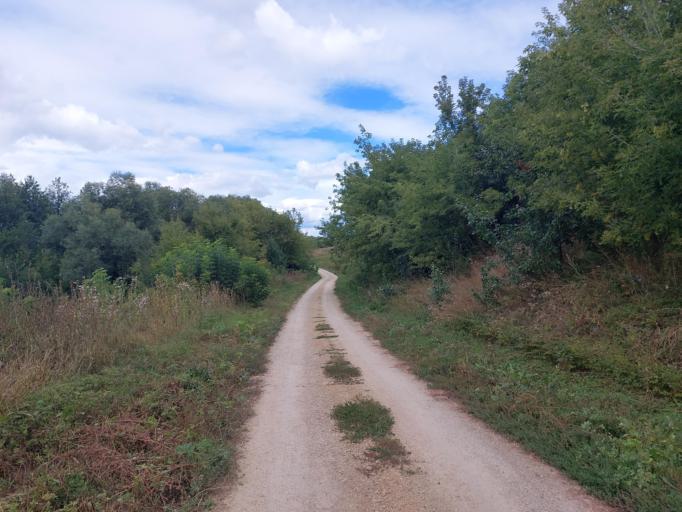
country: RU
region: Lipetsk
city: Terbuny
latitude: 52.2643
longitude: 38.2064
